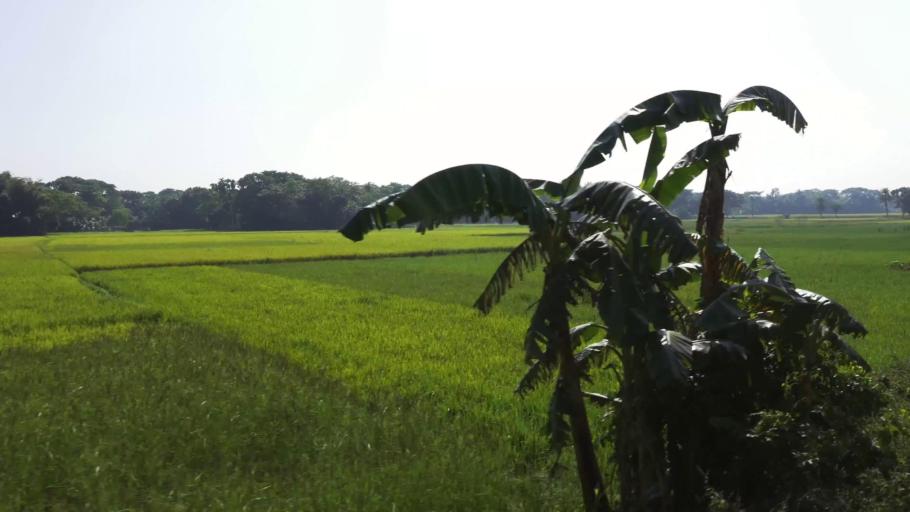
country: BD
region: Dhaka
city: Gafargaon
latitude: 24.5794
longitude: 90.5080
